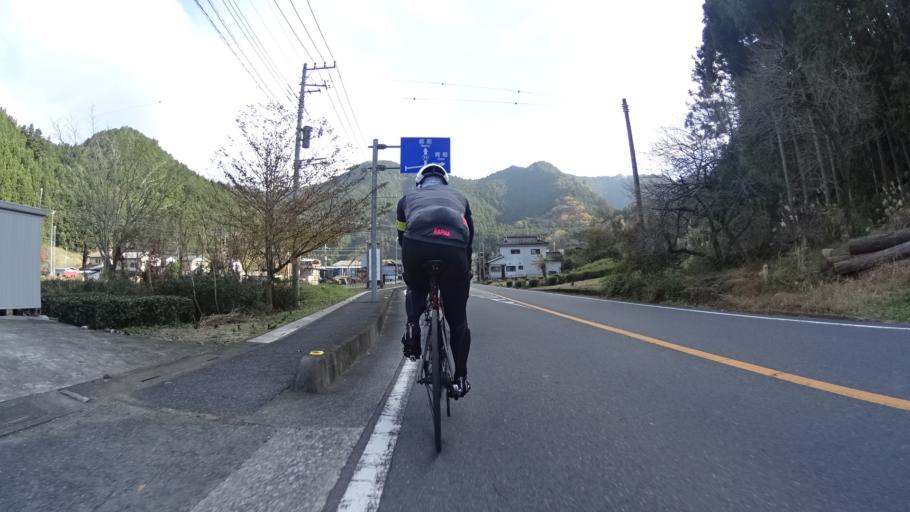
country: JP
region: Tokyo
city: Ome
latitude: 35.8528
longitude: 139.1978
